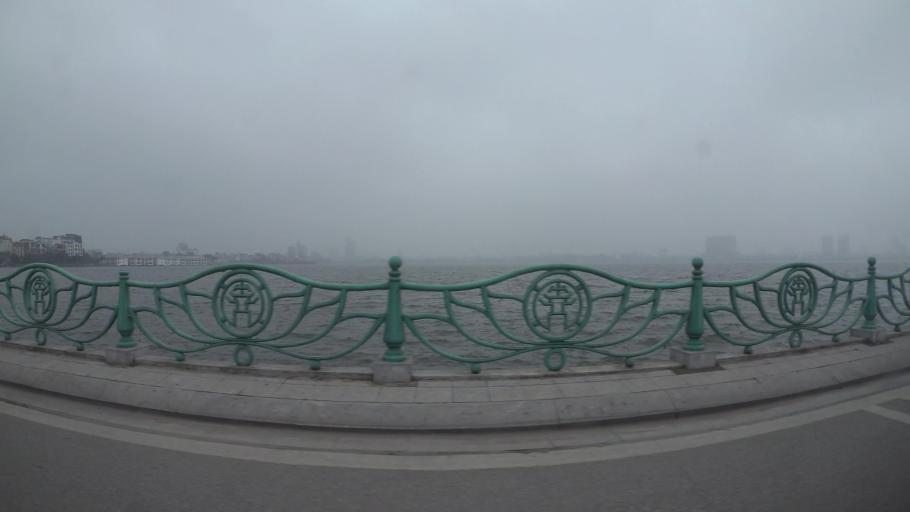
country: VN
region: Ha Noi
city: Tay Ho
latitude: 21.0582
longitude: 105.8252
